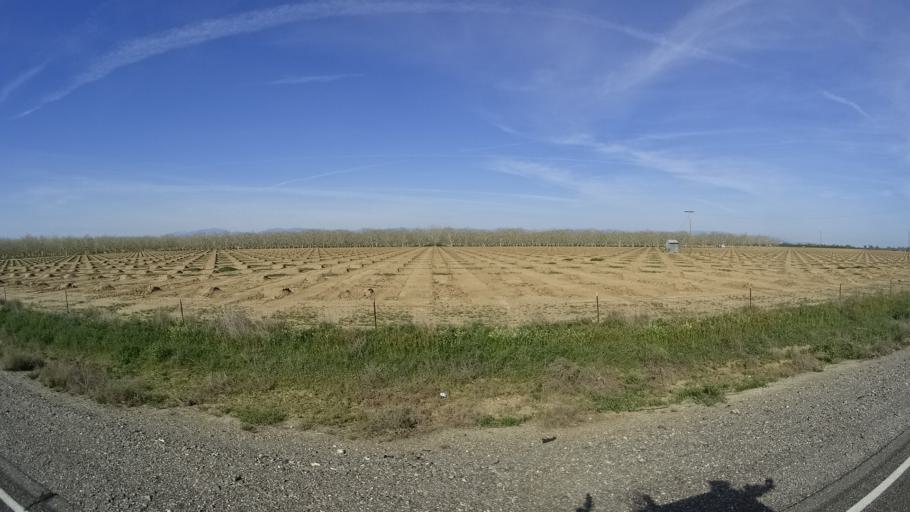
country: US
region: California
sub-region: Glenn County
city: Orland
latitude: 39.6441
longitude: -122.1973
